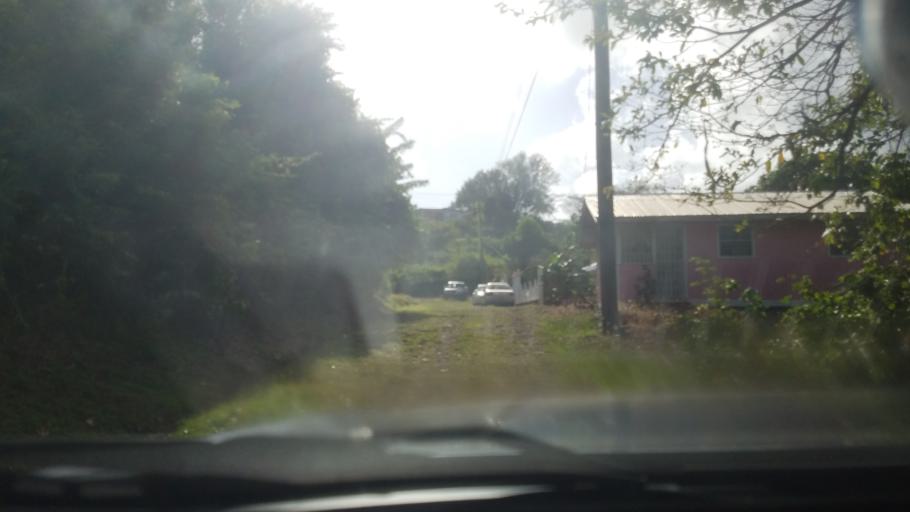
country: LC
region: Gros-Islet
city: Gros Islet
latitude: 14.0643
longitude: -60.9581
